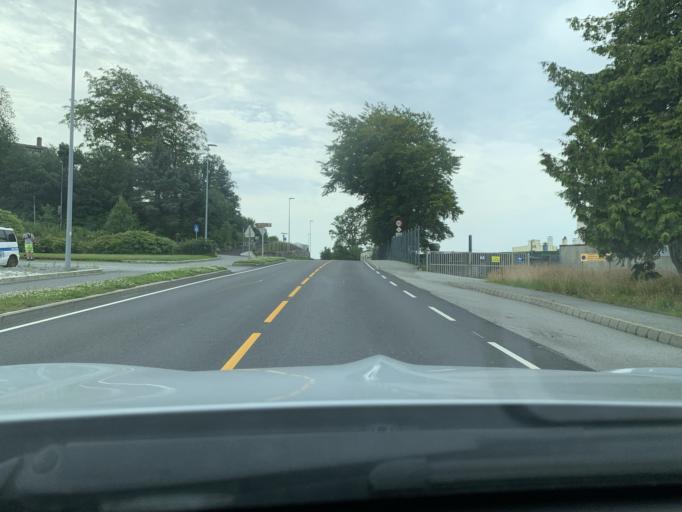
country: NO
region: Rogaland
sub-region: Sandnes
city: Sandnes
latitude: 58.7784
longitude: 5.7208
